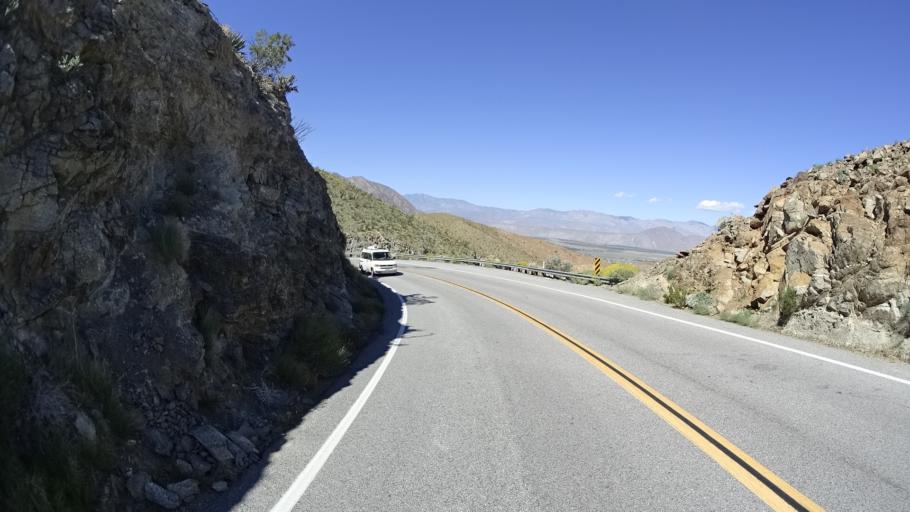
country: US
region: California
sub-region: San Diego County
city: Borrego Springs
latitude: 33.2296
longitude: -116.4110
